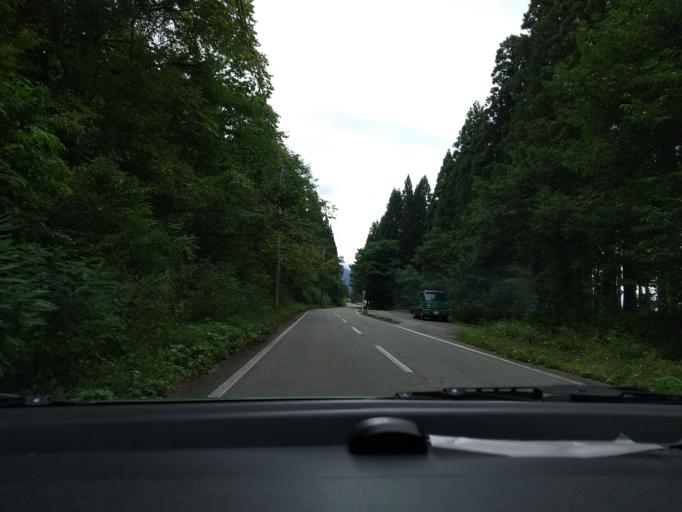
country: JP
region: Akita
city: Kakunodatemachi
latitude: 39.5445
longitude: 140.6371
